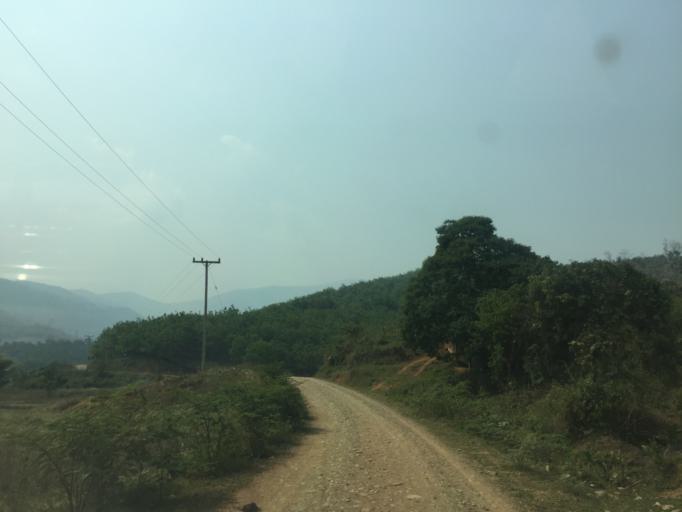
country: TH
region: Phayao
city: Phu Sang
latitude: 19.5736
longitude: 100.5254
